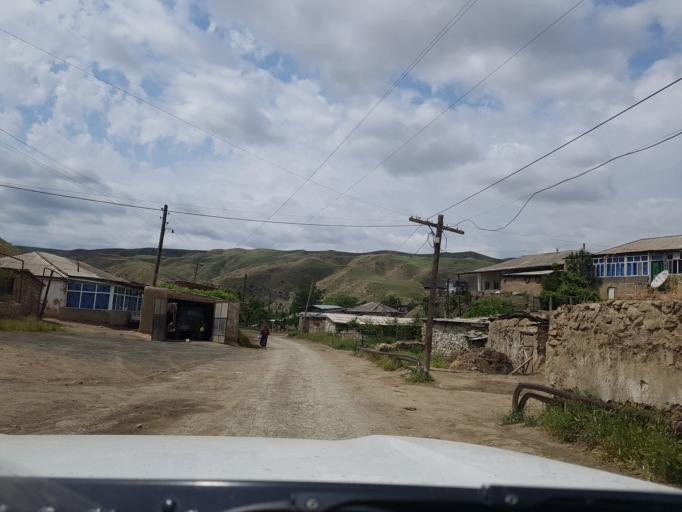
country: TM
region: Ahal
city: Baharly
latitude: 38.2000
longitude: 57.0050
